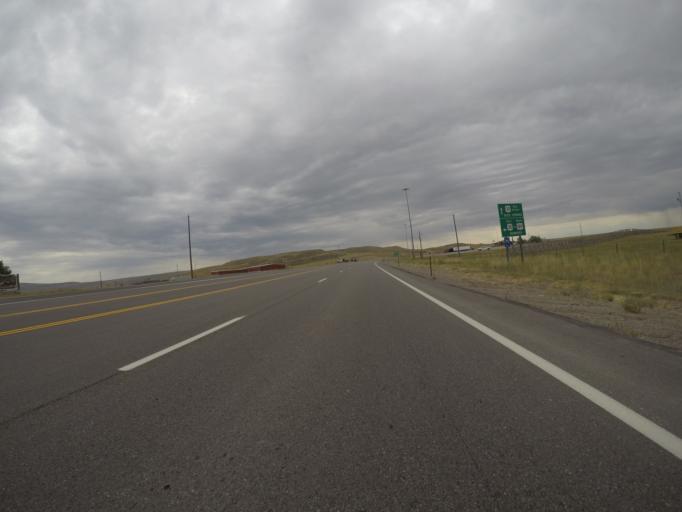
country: US
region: Wyoming
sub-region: Lincoln County
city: Kemmerer
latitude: 41.7932
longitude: -110.5787
